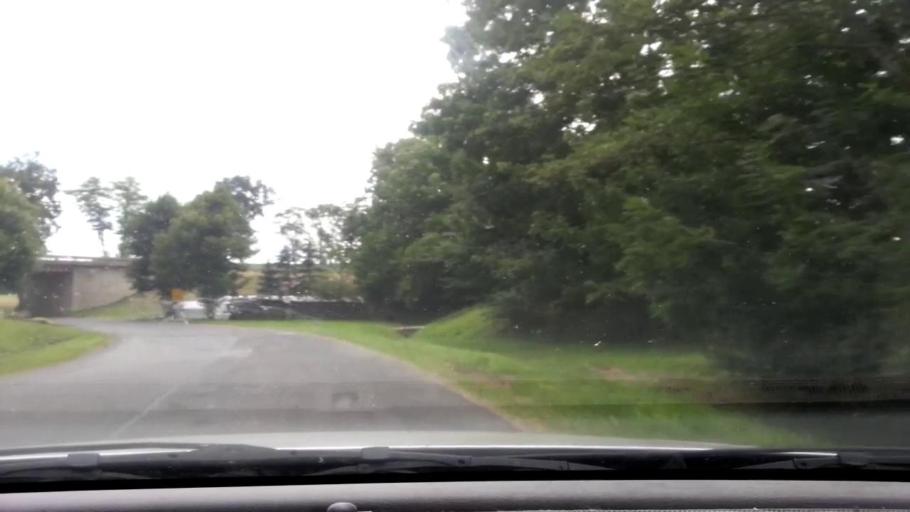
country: DE
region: Bavaria
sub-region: Upper Palatinate
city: Kulmain
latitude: 49.8987
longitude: 11.9246
